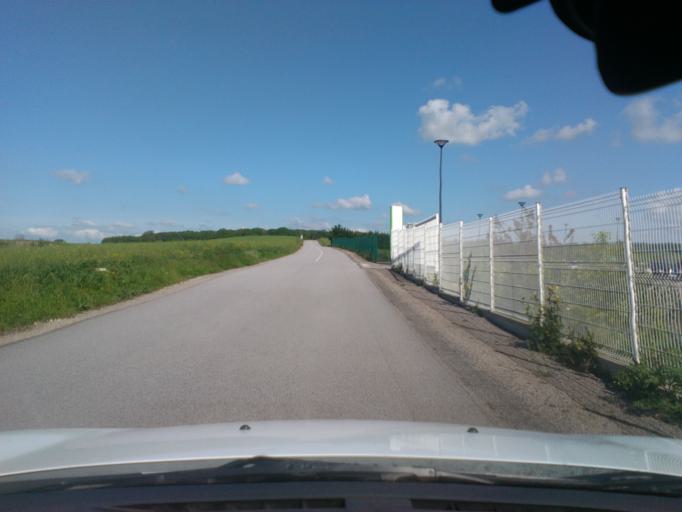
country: FR
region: Lorraine
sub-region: Departement des Vosges
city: Mirecourt
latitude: 48.3307
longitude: 6.1440
